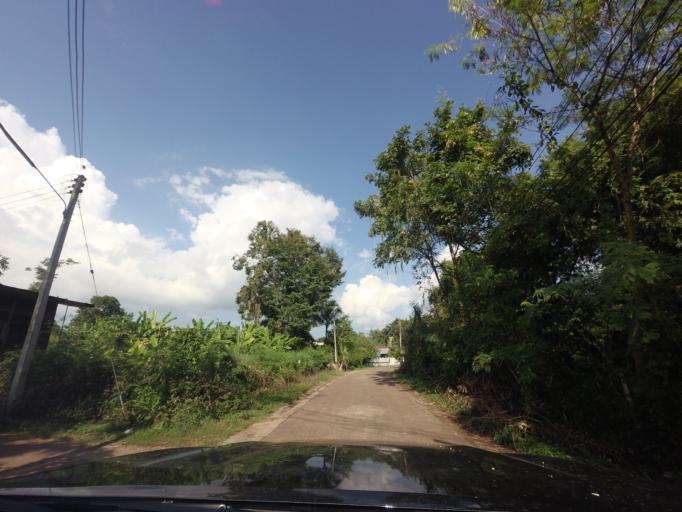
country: TH
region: Nong Khai
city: Nong Khai
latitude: 17.8858
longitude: 102.7705
